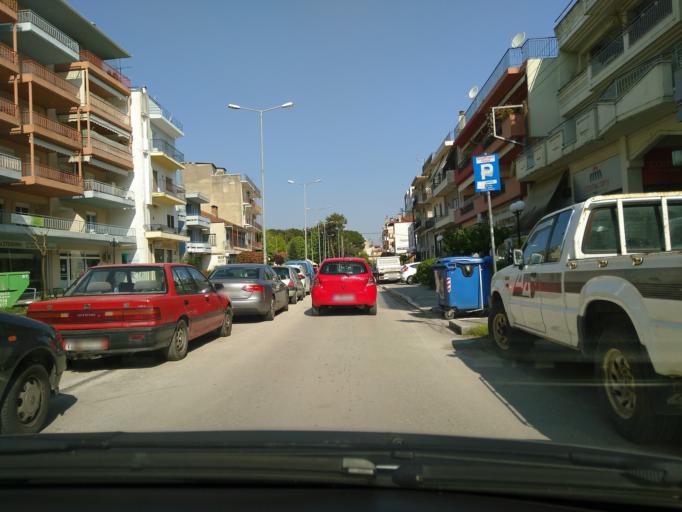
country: GR
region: Epirus
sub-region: Nomos Ioanninon
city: Ioannina
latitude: 39.6725
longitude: 20.8463
